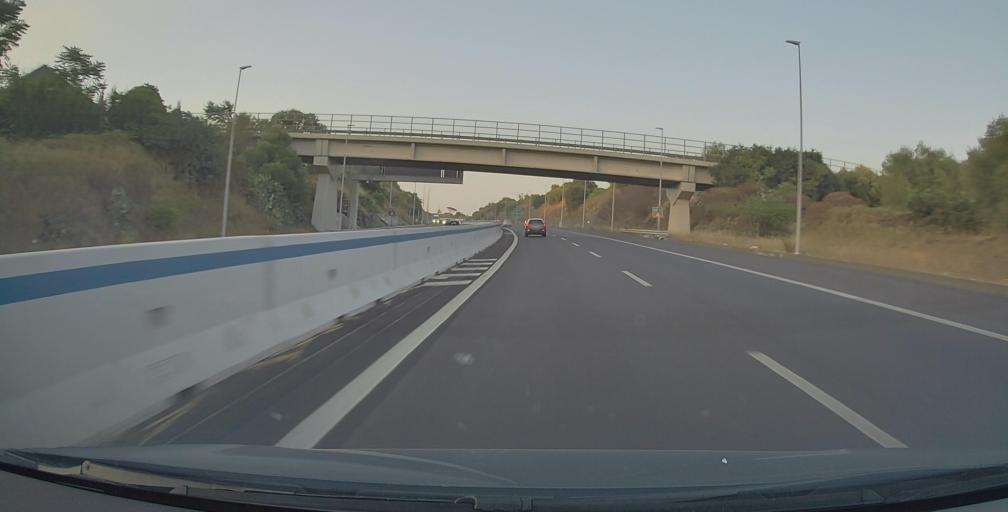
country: IT
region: Sicily
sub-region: Catania
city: Sant'Agata Li Battiati
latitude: 37.5523
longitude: 15.0852
